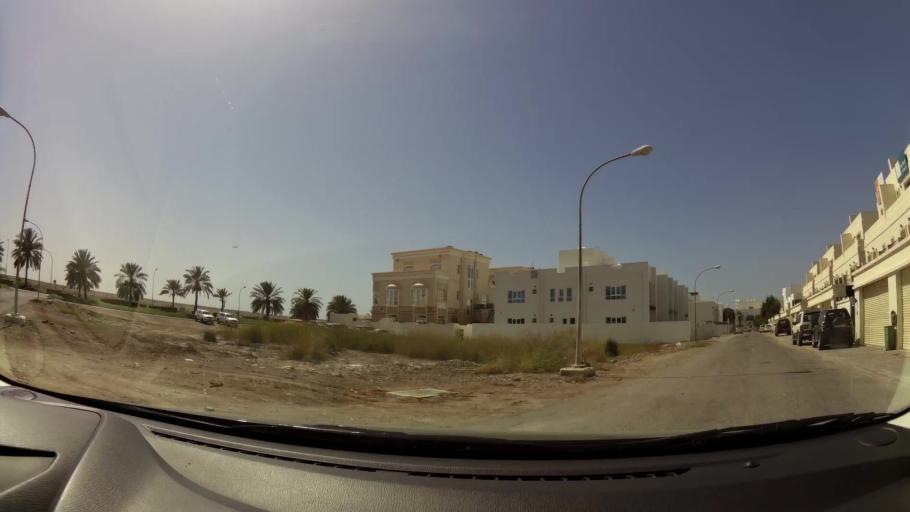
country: OM
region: Muhafazat Masqat
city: Bawshar
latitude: 23.5992
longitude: 58.3478
